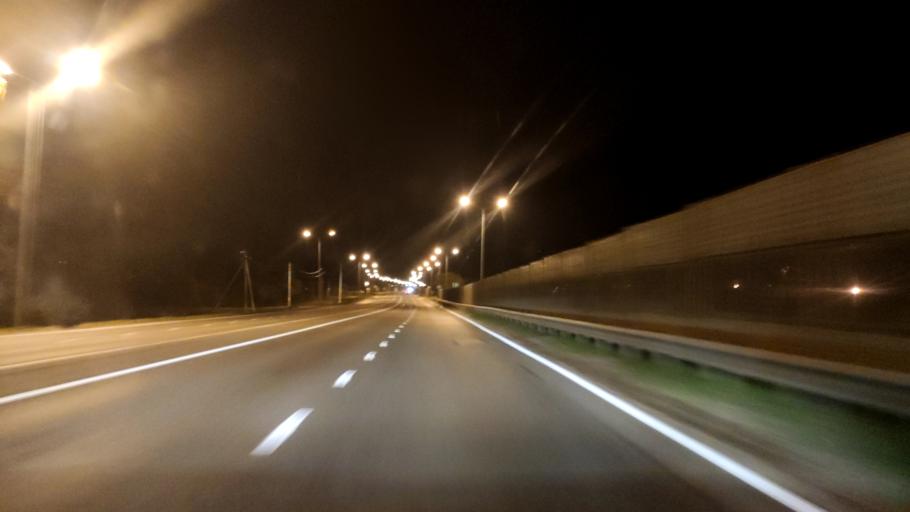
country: RU
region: Belgorod
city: Staryy Oskol
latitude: 51.3410
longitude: 37.8008
